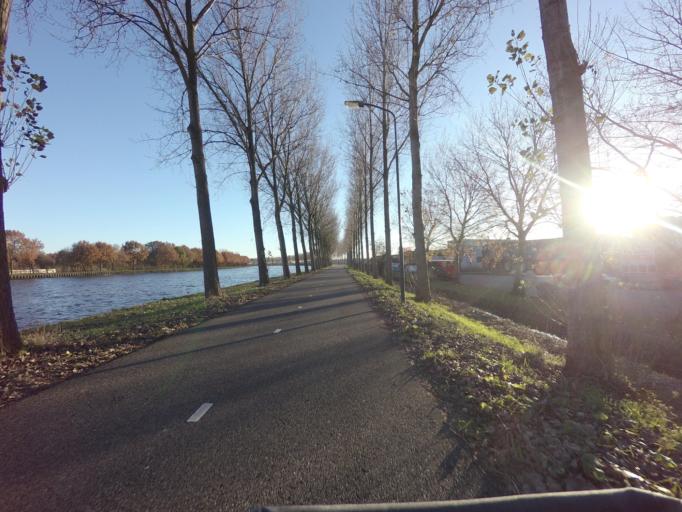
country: NL
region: Utrecht
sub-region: Stichtse Vecht
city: Breukelen
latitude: 52.1636
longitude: 4.9953
